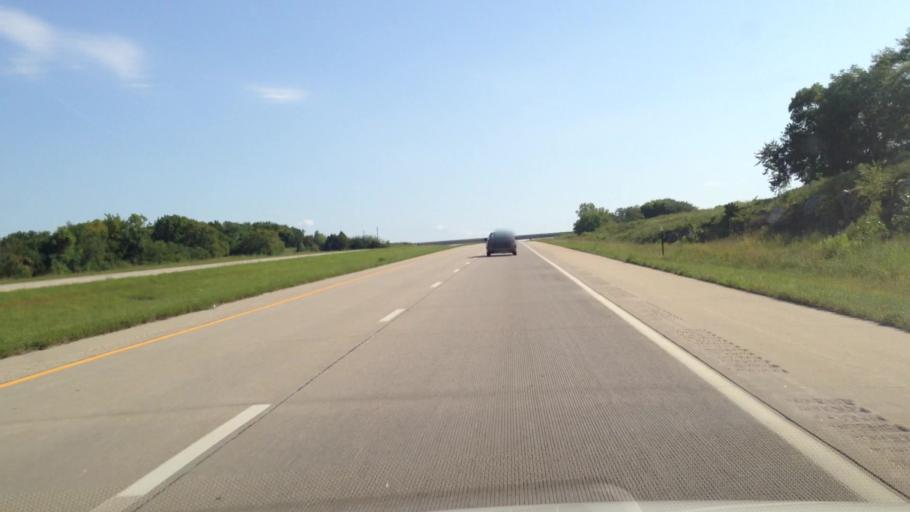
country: US
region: Kansas
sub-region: Linn County
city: Pleasanton
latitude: 38.1156
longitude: -94.7137
